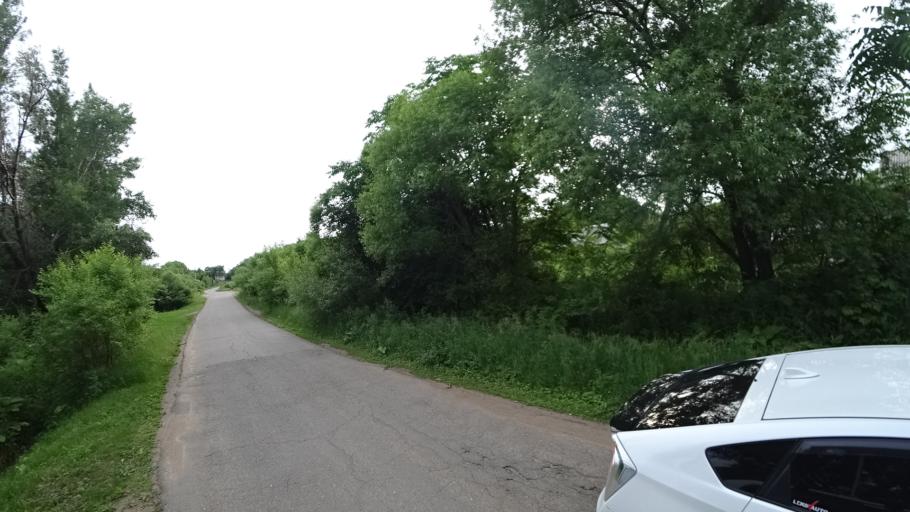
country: RU
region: Primorskiy
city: Novosysoyevka
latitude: 44.2461
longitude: 133.3715
